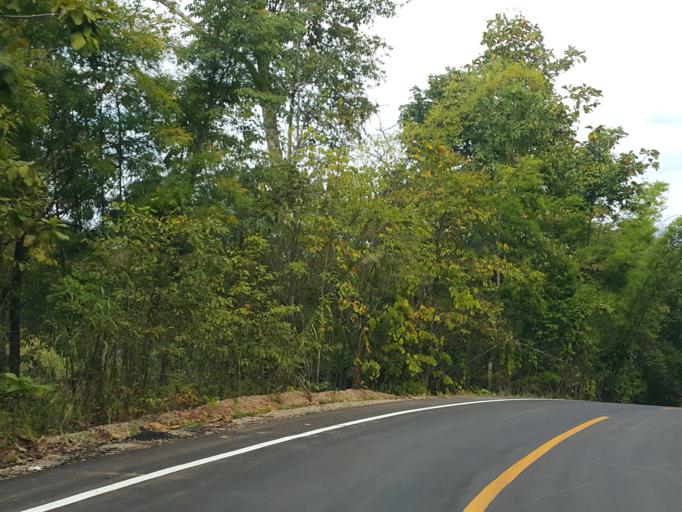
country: TH
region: Lampang
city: Chae Hom
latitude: 18.6517
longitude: 99.5167
